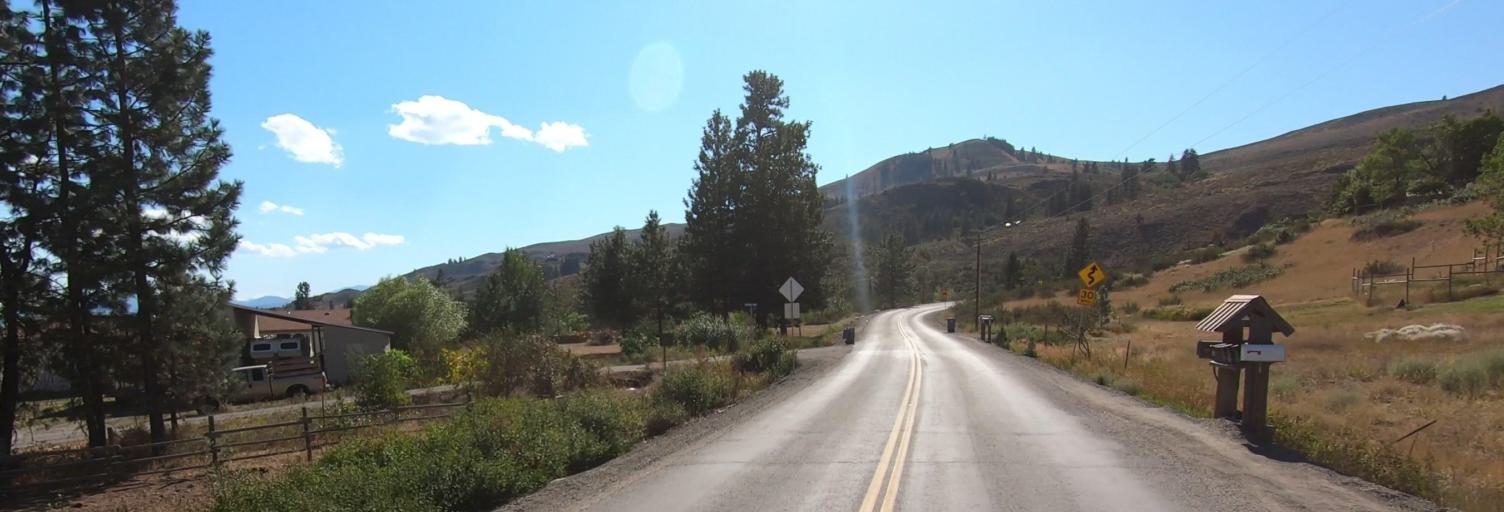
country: US
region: Washington
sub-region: Okanogan County
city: Brewster
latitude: 48.5526
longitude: -120.1888
